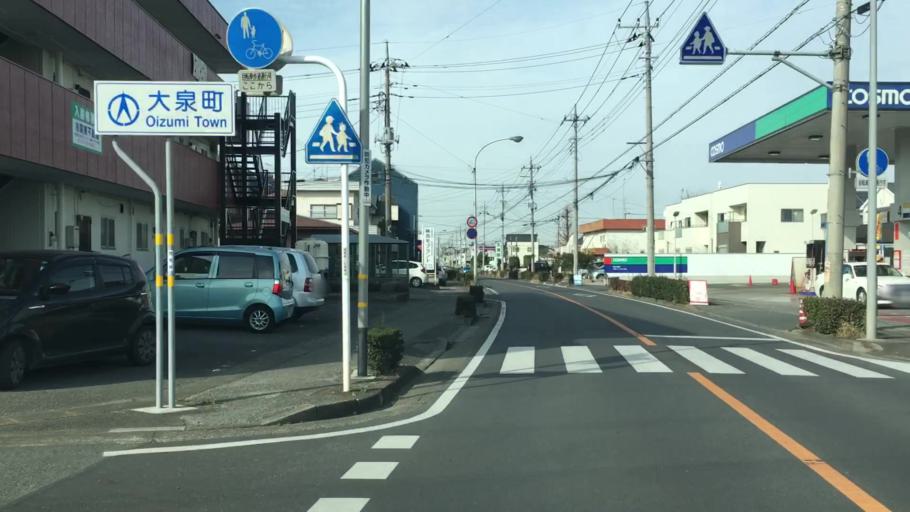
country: JP
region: Saitama
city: Menuma
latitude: 36.2507
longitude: 139.4287
